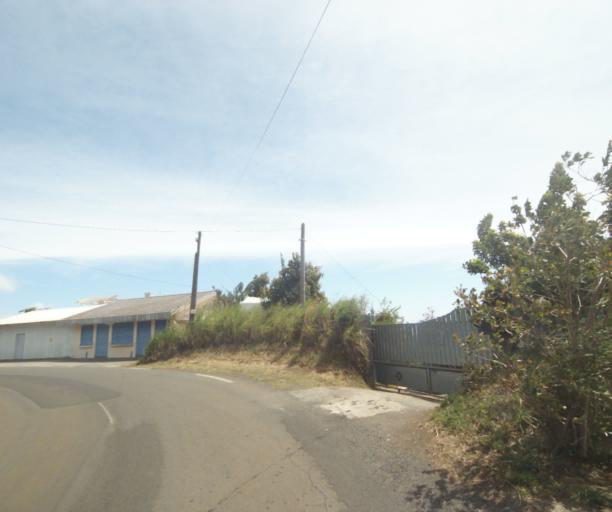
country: RE
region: Reunion
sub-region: Reunion
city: Trois-Bassins
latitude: -21.0647
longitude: 55.3072
